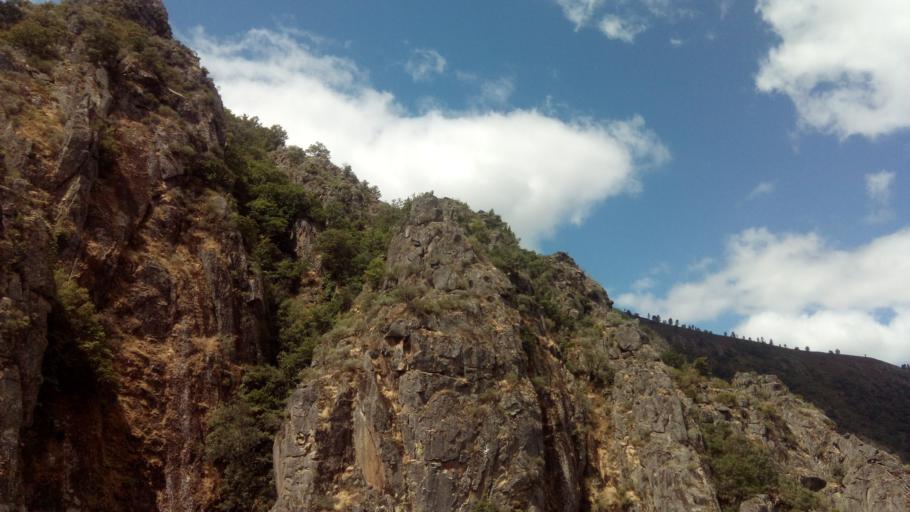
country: ES
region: Galicia
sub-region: Provincia de Lugo
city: Sober
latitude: 42.3905
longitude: -7.6219
